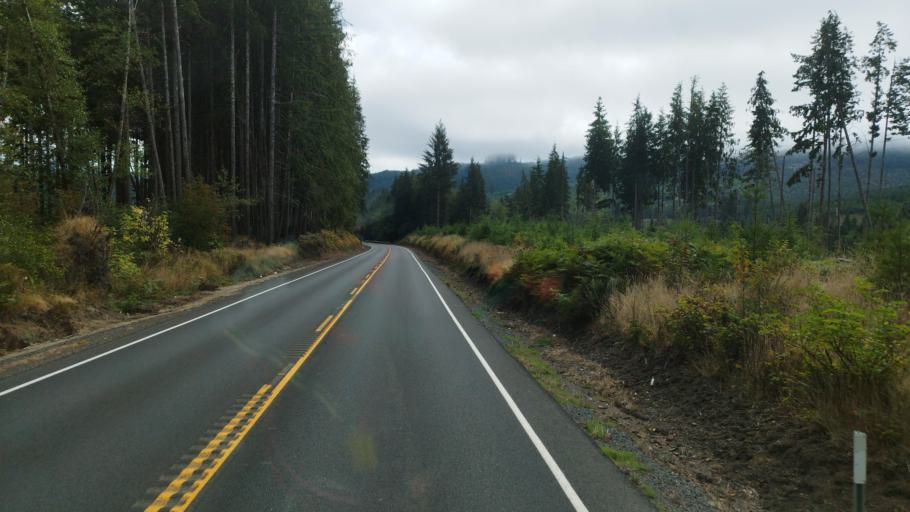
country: US
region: Oregon
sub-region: Clatsop County
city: Seaside
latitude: 45.8989
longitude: -123.6538
